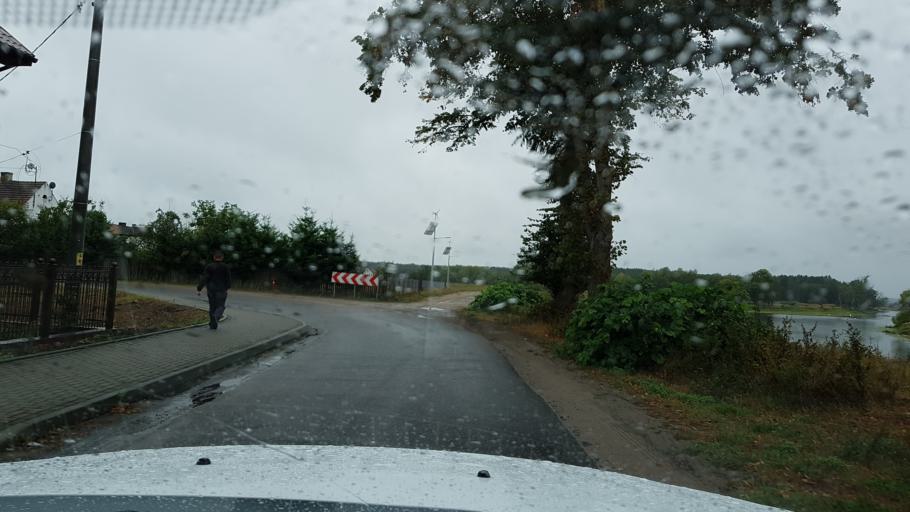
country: DE
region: Brandenburg
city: Schoneberg
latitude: 52.9785
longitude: 14.2062
